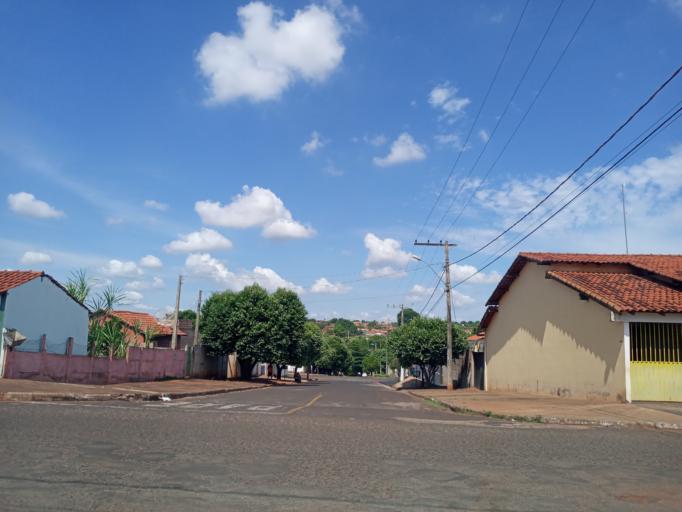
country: BR
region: Minas Gerais
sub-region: Ituiutaba
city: Ituiutaba
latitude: -18.9868
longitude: -49.4724
